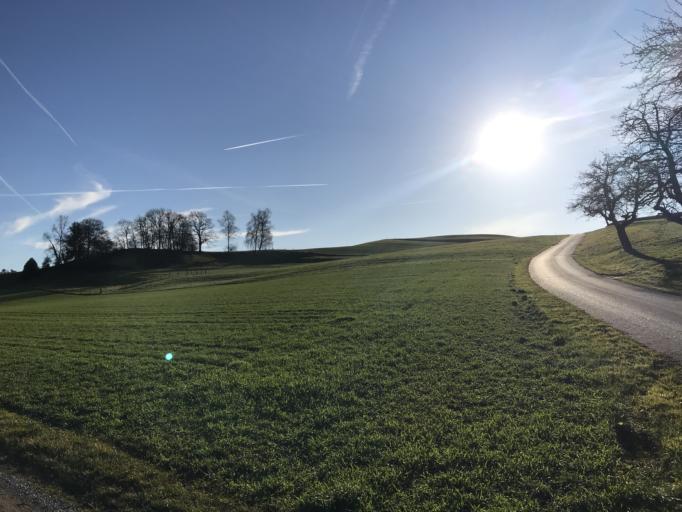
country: CH
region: Schaffhausen
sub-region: Bezirk Stein
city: Stein am Rhein
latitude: 47.6387
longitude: 8.8547
